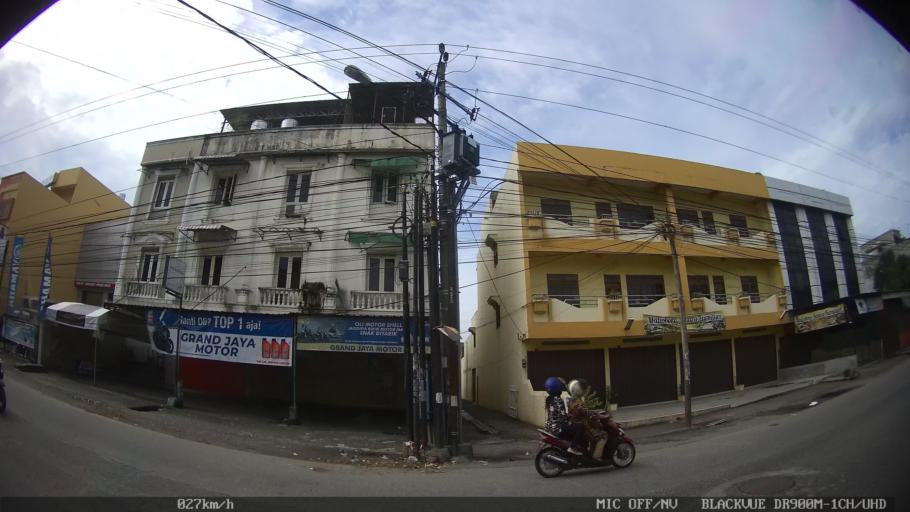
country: ID
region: North Sumatra
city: Medan
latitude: 3.6232
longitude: 98.6794
